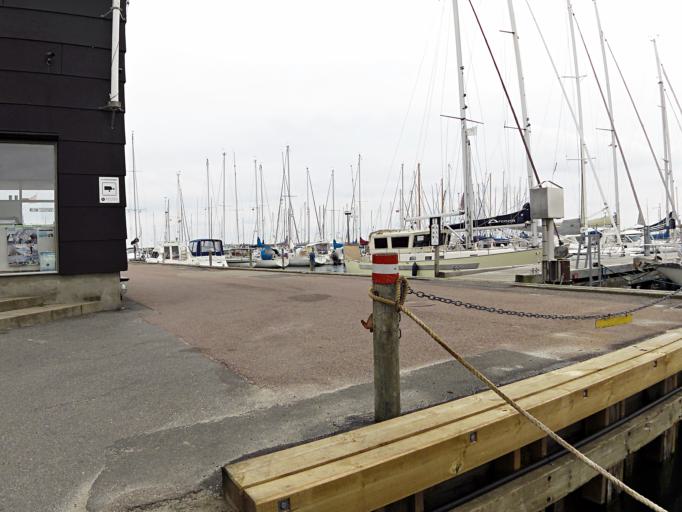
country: DK
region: Capital Region
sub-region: Rudersdal Kommune
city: Trorod
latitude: 55.8490
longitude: 12.5714
